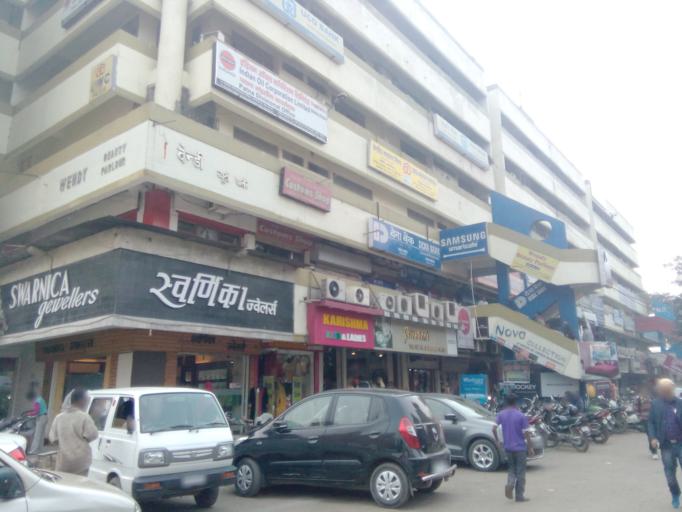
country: IN
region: Bihar
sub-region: Patna
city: Patna
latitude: 25.6101
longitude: 85.1349
